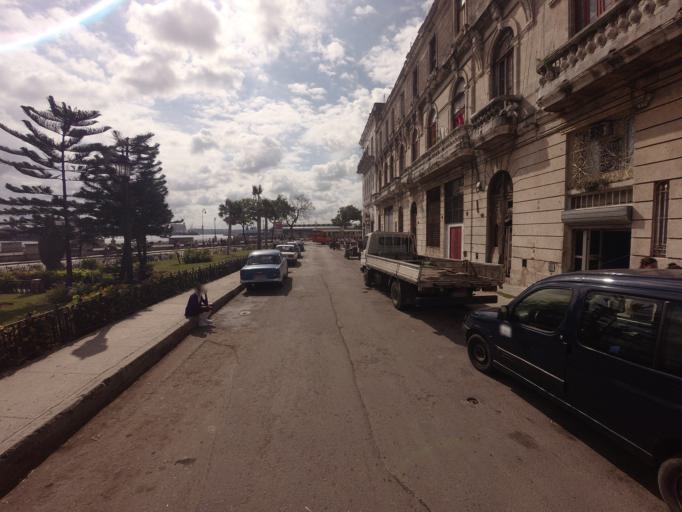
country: CU
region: La Habana
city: La Habana Vieja
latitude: 23.1335
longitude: -82.3480
